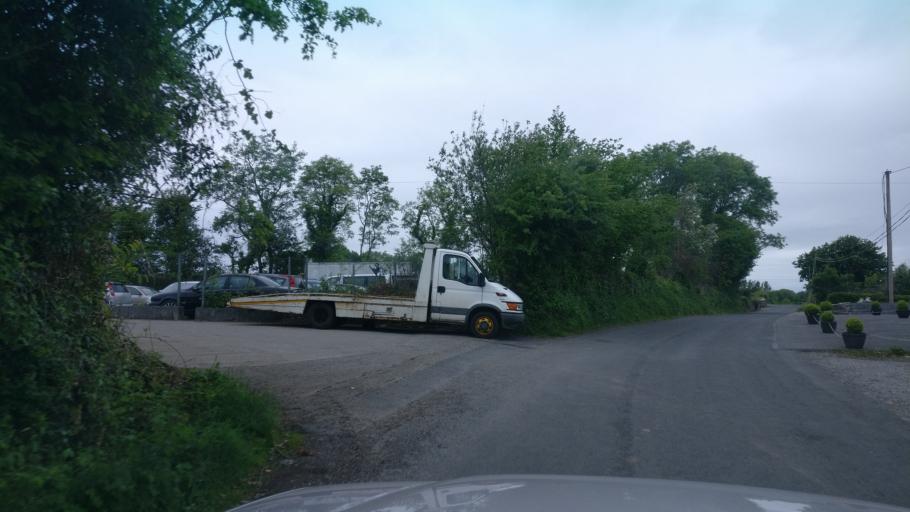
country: IE
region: Connaught
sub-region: County Galway
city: Loughrea
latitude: 53.1116
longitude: -8.4089
